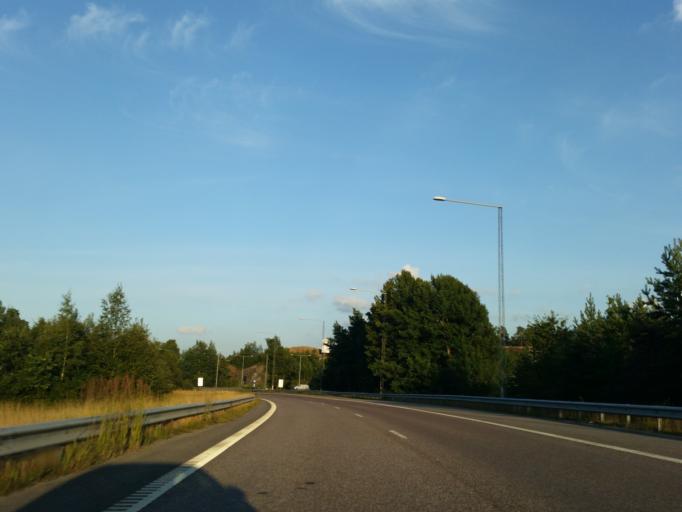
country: SE
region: Stockholm
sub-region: Sodertalje Kommun
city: Soedertaelje
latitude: 59.1998
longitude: 17.6596
